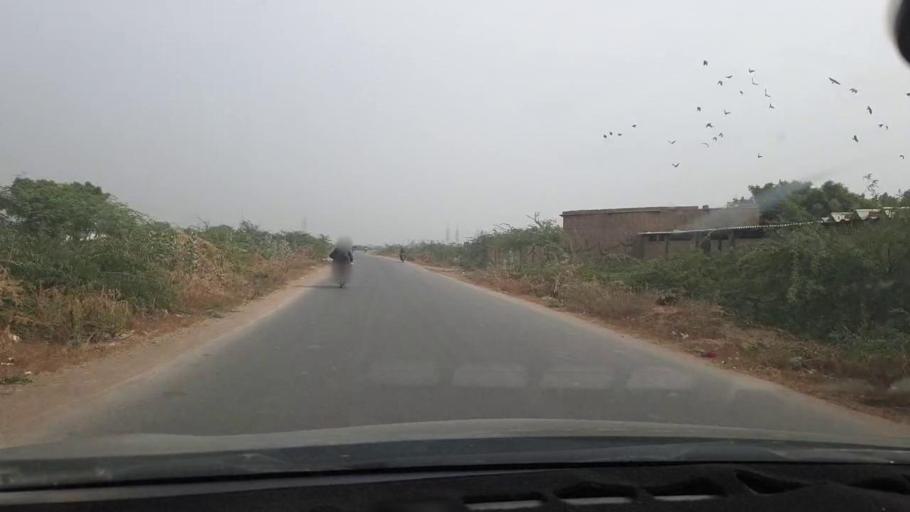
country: PK
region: Sindh
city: Malir Cantonment
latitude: 24.9137
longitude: 67.2723
